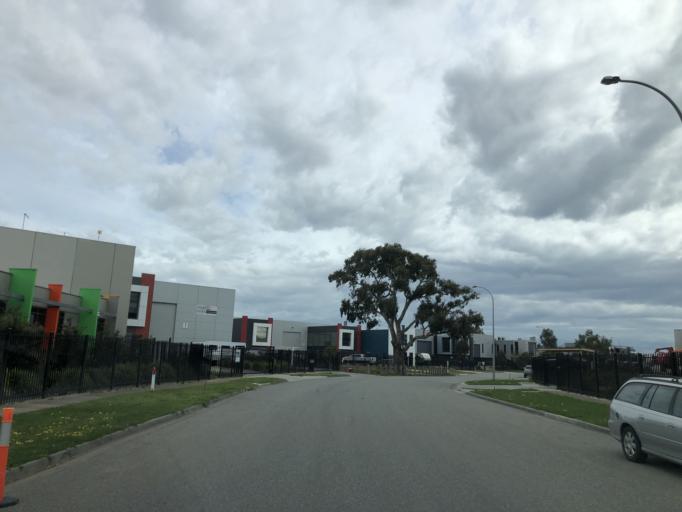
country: AU
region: Victoria
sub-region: Frankston
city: Carrum Downs
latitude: -38.0902
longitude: 145.1702
